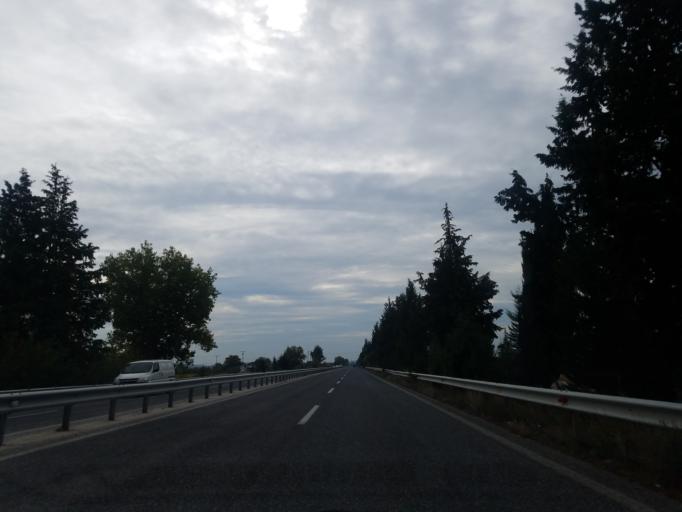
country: GR
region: Thessaly
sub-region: Trikala
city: Vasiliki
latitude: 39.6448
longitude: 21.6899
